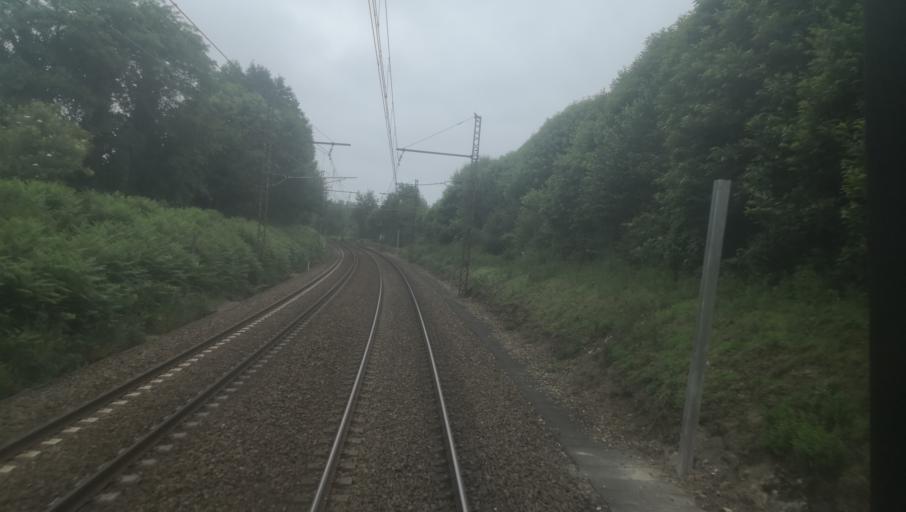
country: FR
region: Limousin
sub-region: Departement de la Creuse
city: La Souterraine
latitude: 46.2281
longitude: 1.4964
